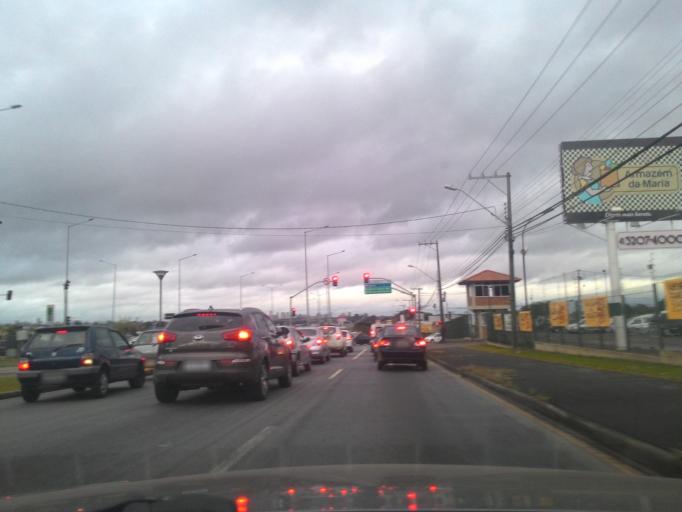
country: BR
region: Parana
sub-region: Curitiba
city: Curitiba
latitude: -25.4849
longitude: -49.2662
